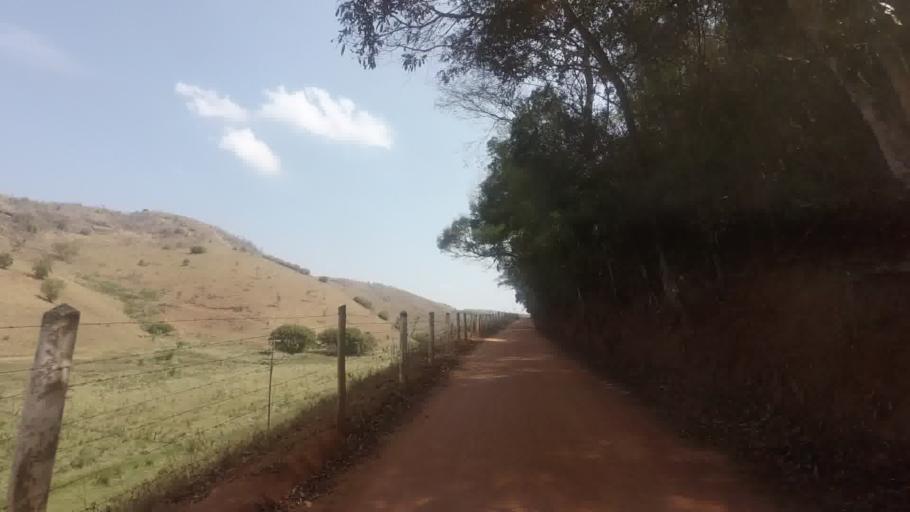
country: BR
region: Espirito Santo
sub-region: Sao Jose Do Calcado
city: Sao Jose do Calcado
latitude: -21.0538
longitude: -41.5304
